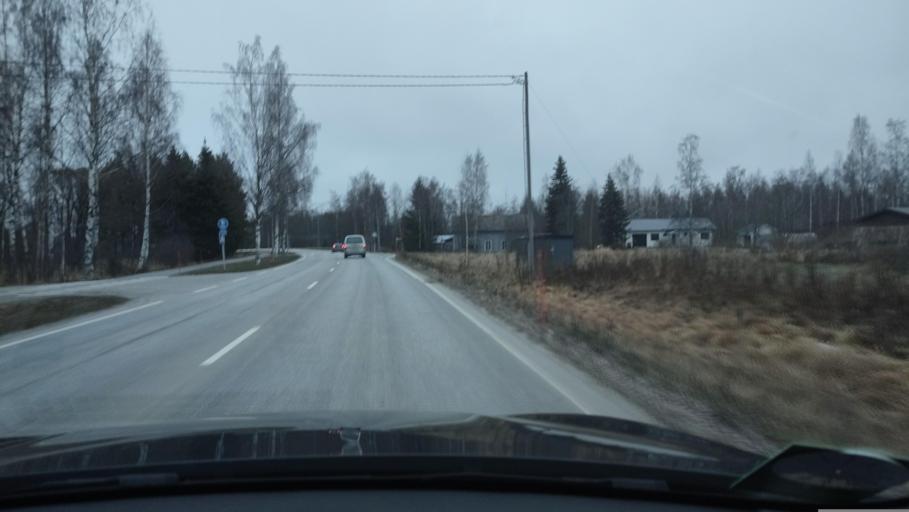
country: FI
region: Southern Ostrobothnia
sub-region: Suupohja
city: Kauhajoki
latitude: 62.4437
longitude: 22.2010
